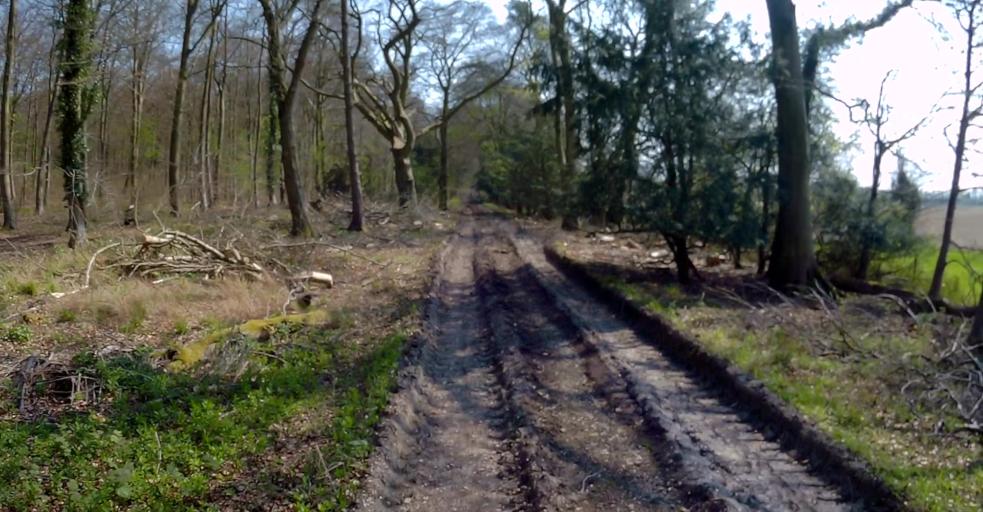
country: GB
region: England
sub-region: Hampshire
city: Overton
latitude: 51.1871
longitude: -1.2455
